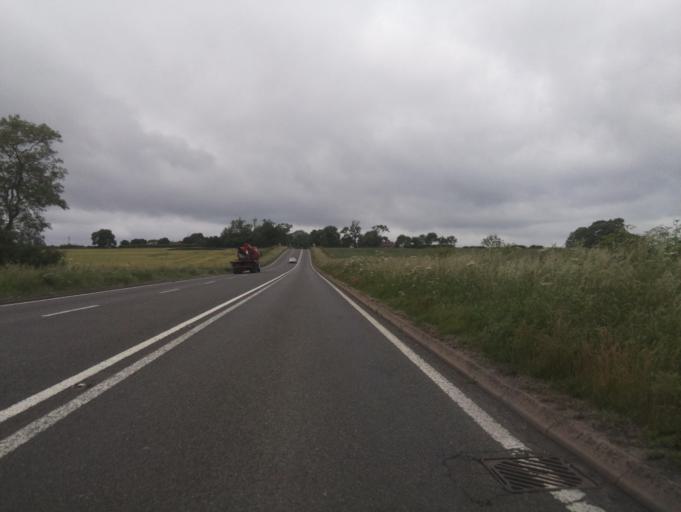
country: GB
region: England
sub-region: Leicestershire
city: Houghton on the Hill
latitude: 52.6079
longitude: -0.8831
